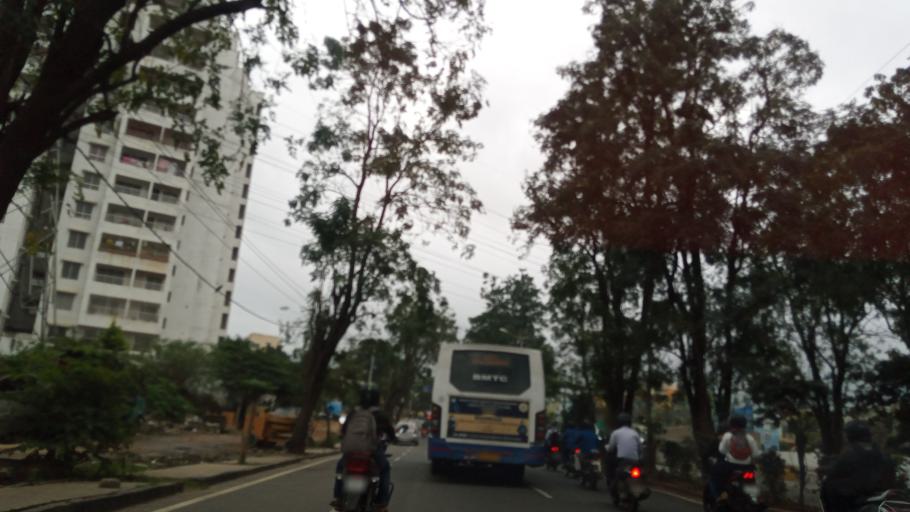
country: IN
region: Karnataka
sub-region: Bangalore Urban
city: Bangalore
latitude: 12.9360
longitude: 77.5351
